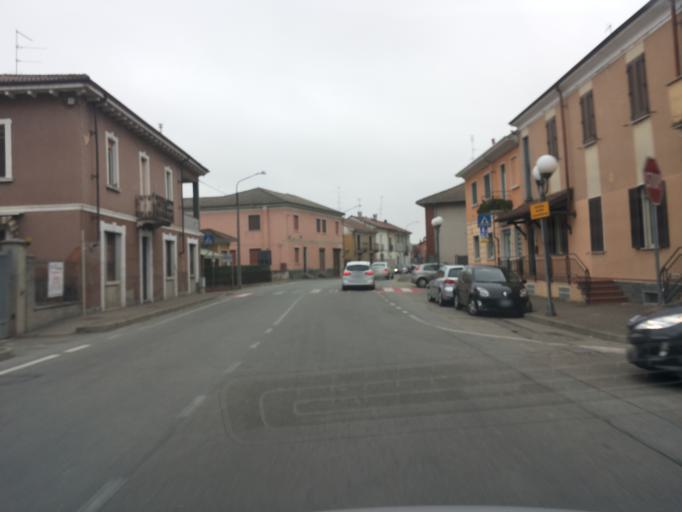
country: IT
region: Piedmont
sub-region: Provincia di Novara
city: Casalino
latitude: 45.3967
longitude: 8.5359
